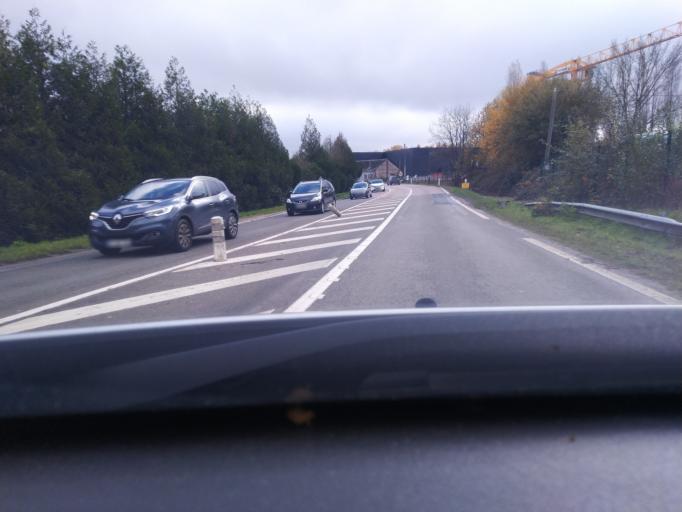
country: FR
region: Haute-Normandie
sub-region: Departement de la Seine-Maritime
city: Maromme
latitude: 49.4882
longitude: 1.0176
